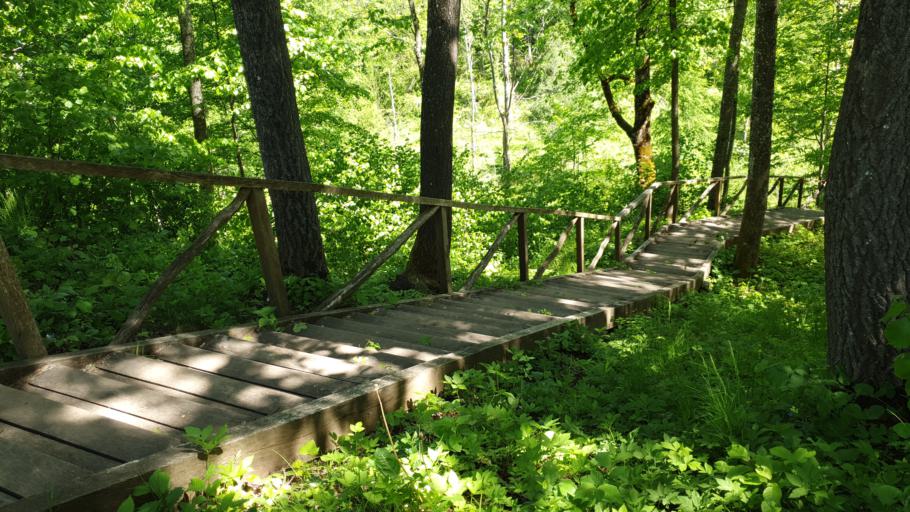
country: LT
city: Moletai
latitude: 55.0732
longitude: 25.4130
